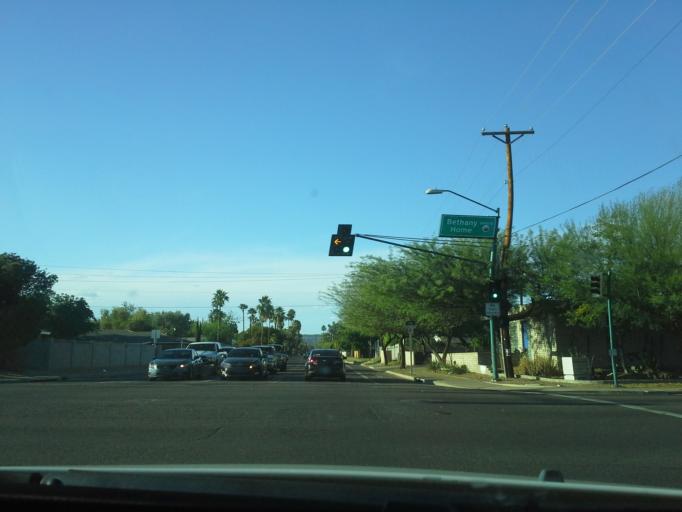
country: US
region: Arizona
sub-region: Maricopa County
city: Phoenix
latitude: 33.5238
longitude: -112.0911
